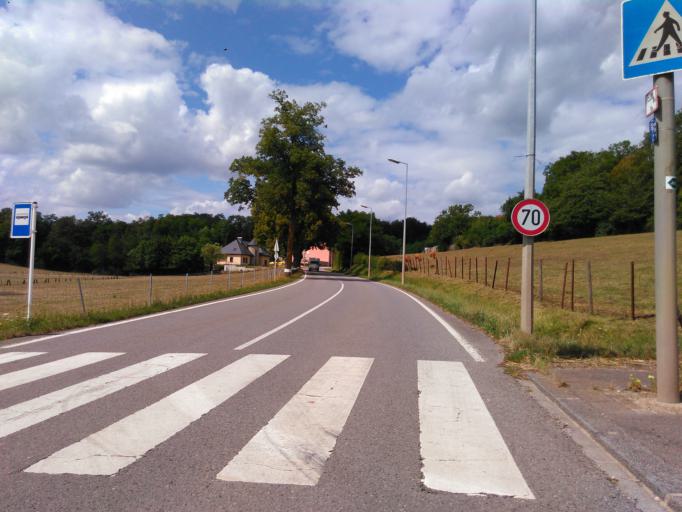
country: LU
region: Grevenmacher
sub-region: Canton de Grevenmacher
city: Junglinster
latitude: 49.7301
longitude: 6.3033
